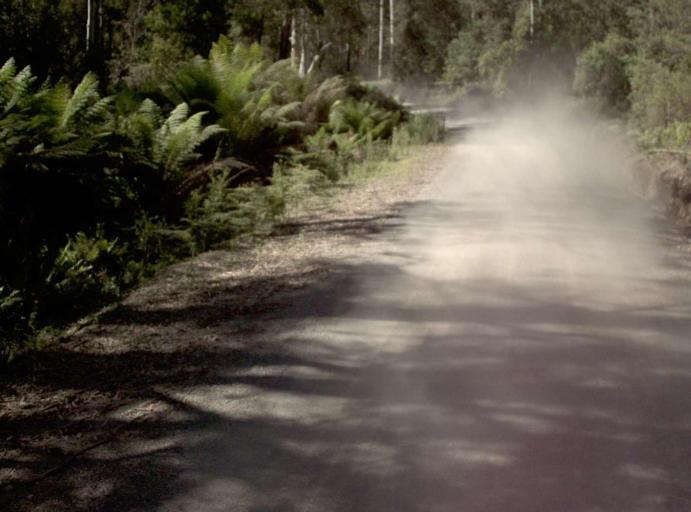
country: AU
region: New South Wales
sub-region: Bombala
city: Bombala
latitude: -37.2204
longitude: 148.7471
